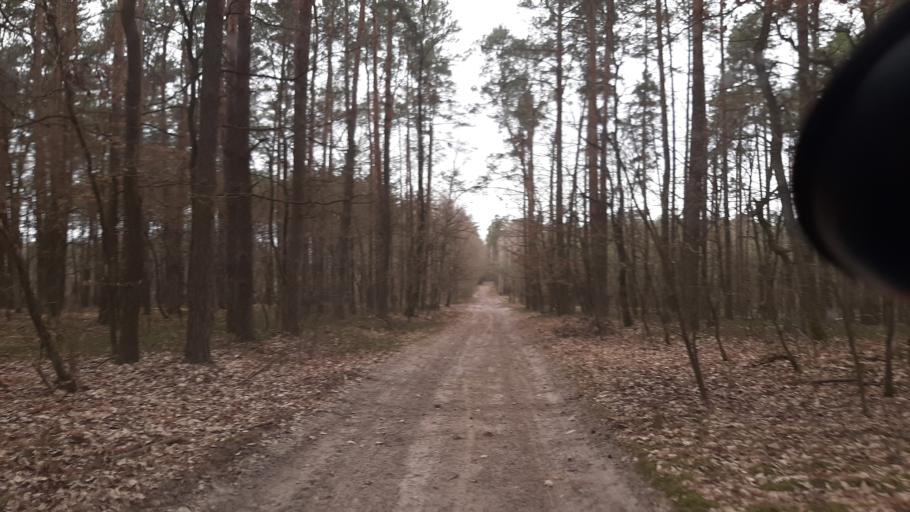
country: PL
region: Lublin Voivodeship
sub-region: Powiat lubelski
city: Garbow
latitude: 51.4006
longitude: 22.3703
